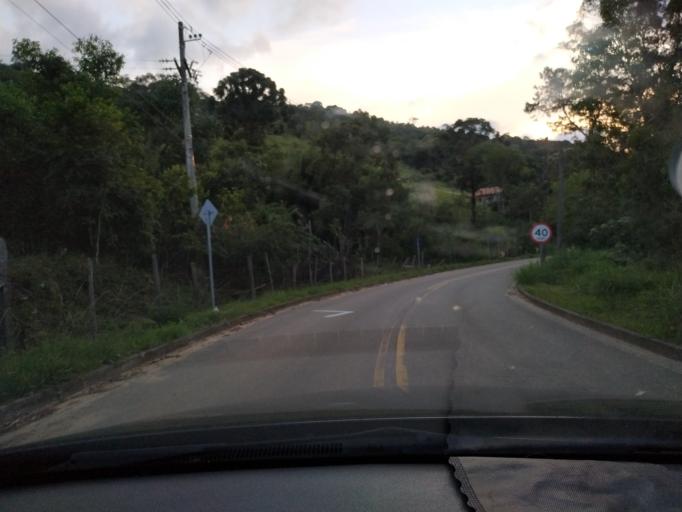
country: BR
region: Sao Paulo
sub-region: Campos Do Jordao
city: Campos do Jordao
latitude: -22.8112
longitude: -45.6472
